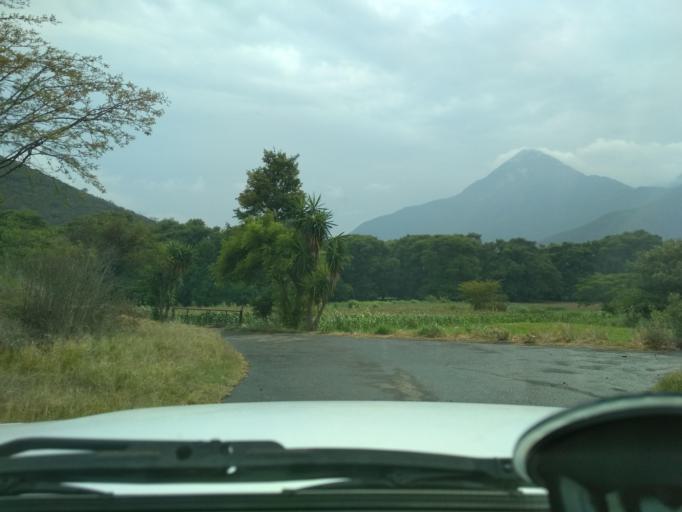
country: MX
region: Veracruz
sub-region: Nogales
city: Taza de Agua Ojo Zarco
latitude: 18.7773
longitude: -97.2043
